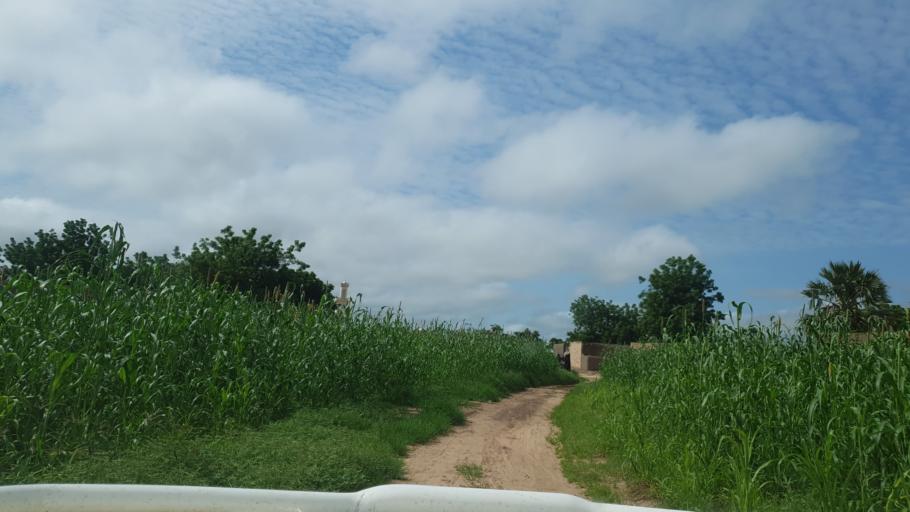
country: ML
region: Segou
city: Baroueli
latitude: 13.4856
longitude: -6.8961
